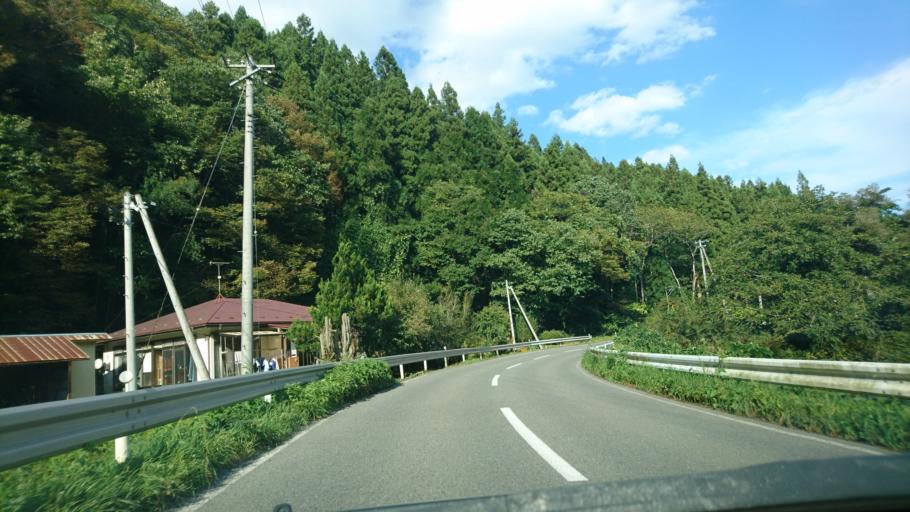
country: JP
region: Iwate
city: Ichinoseki
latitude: 38.8590
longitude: 141.3144
